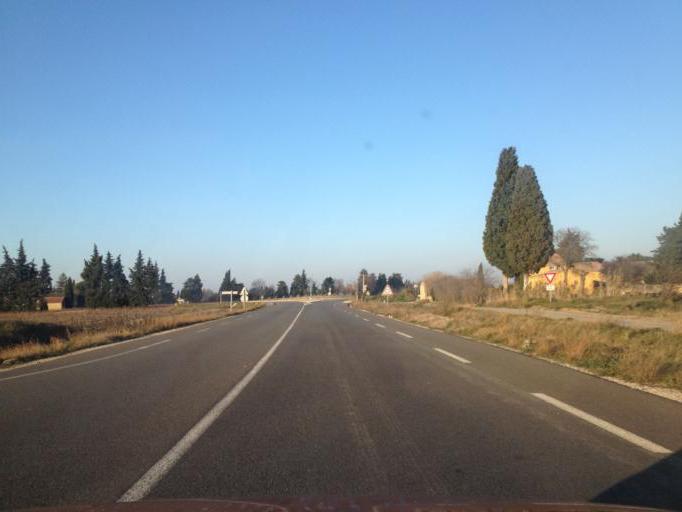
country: FR
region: Provence-Alpes-Cote d'Azur
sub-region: Departement du Vaucluse
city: Camaret-sur-Aigues
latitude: 44.1615
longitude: 4.8872
